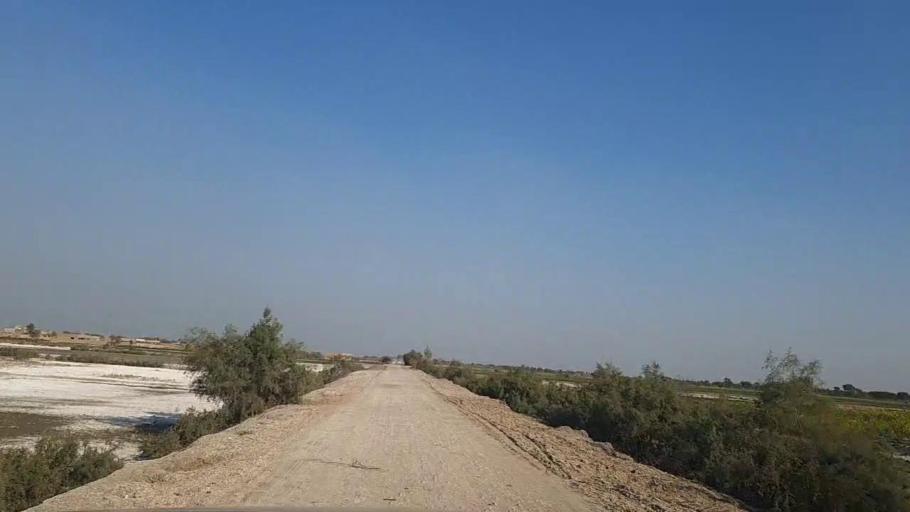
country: PK
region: Sindh
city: Daur
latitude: 26.3178
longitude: 68.1851
